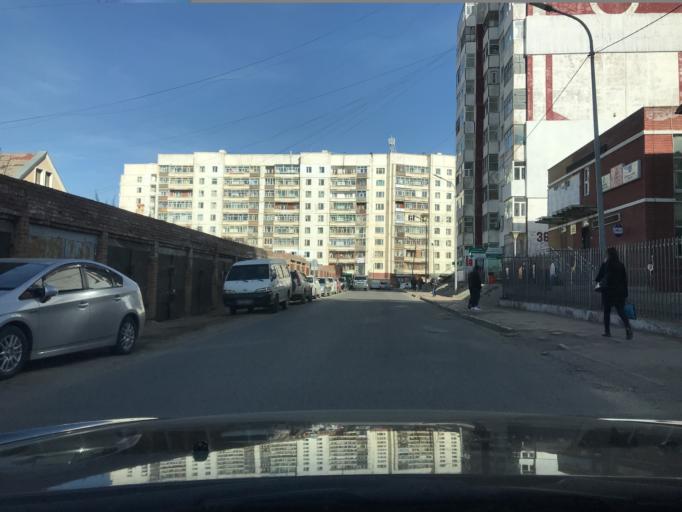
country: MN
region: Ulaanbaatar
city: Ulaanbaatar
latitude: 47.9118
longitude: 106.9383
